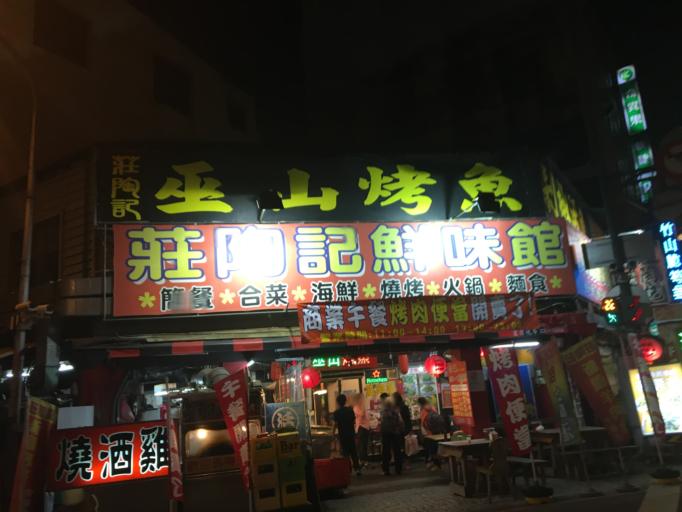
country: TW
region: Taiwan
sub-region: Taichung City
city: Taichung
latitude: 24.1432
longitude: 120.6785
